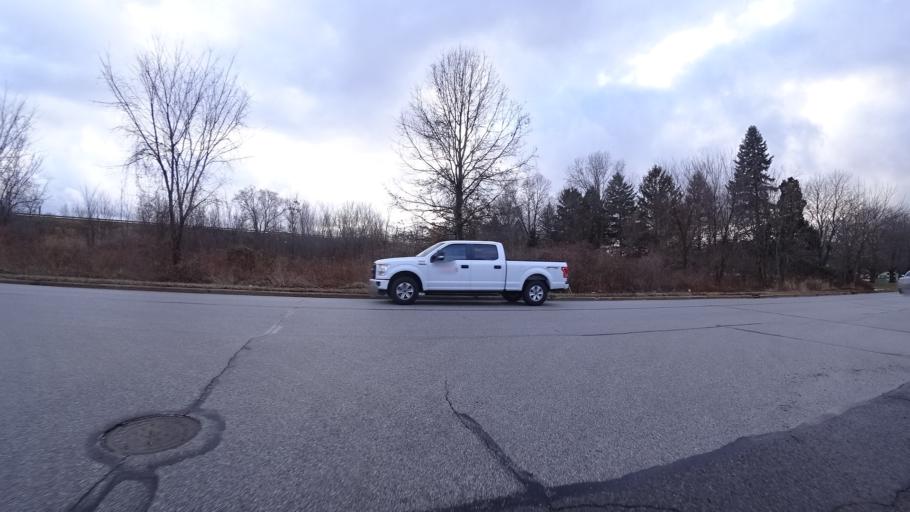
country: US
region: Indiana
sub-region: Porter County
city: Porter
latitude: 41.6168
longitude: -87.0846
